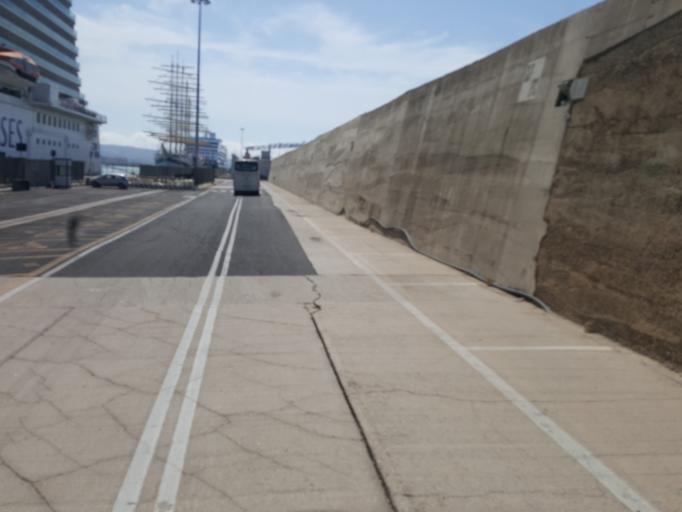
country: IT
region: Latium
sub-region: Citta metropolitana di Roma Capitale
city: Civitavecchia
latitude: 42.0981
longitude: 11.7750
